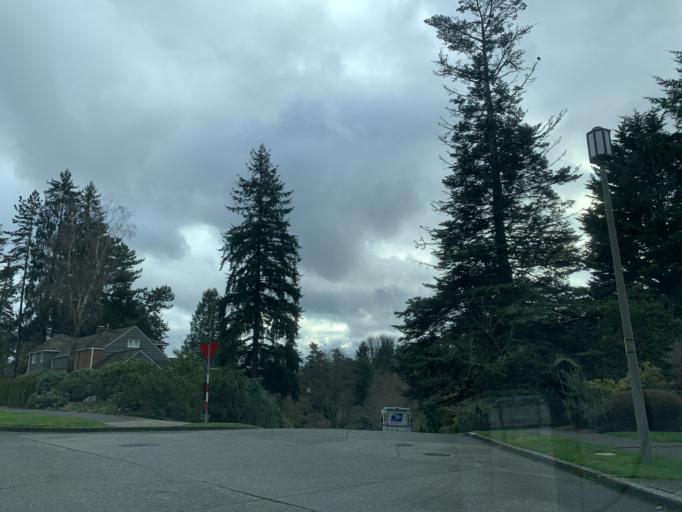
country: US
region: Washington
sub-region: King County
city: Yarrow Point
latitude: 47.6685
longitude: -122.2688
